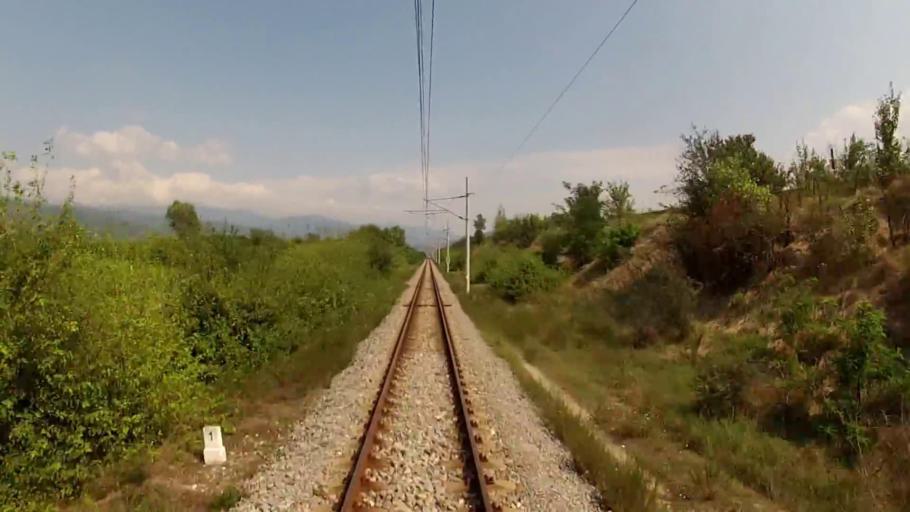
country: BG
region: Blagoevgrad
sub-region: Obshtina Strumyani
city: Strumyani
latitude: 41.6652
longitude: 23.1812
